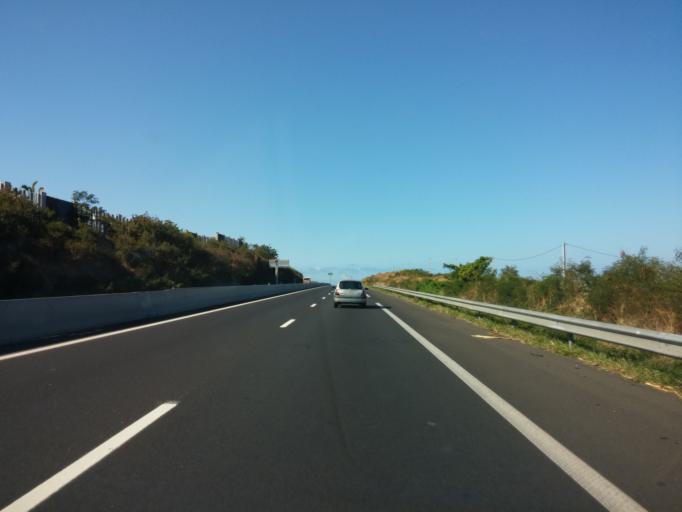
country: RE
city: Piton Saint-Leu
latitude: -21.2100
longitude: 55.2936
